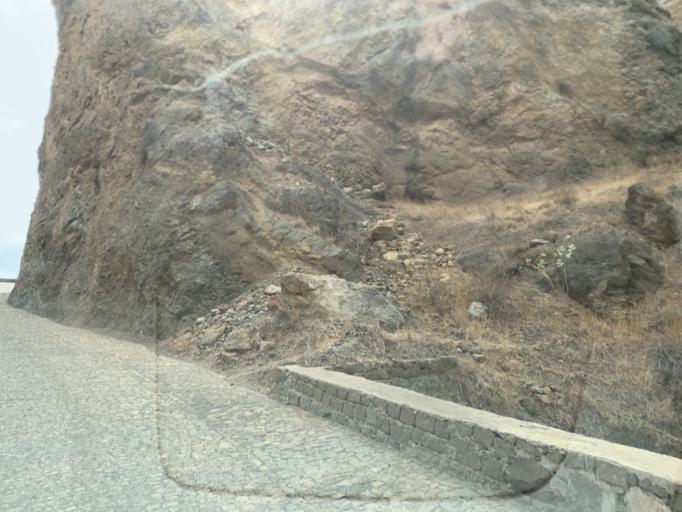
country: CV
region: Brava
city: Vila Nova Sintra
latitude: 14.8745
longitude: -24.7307
